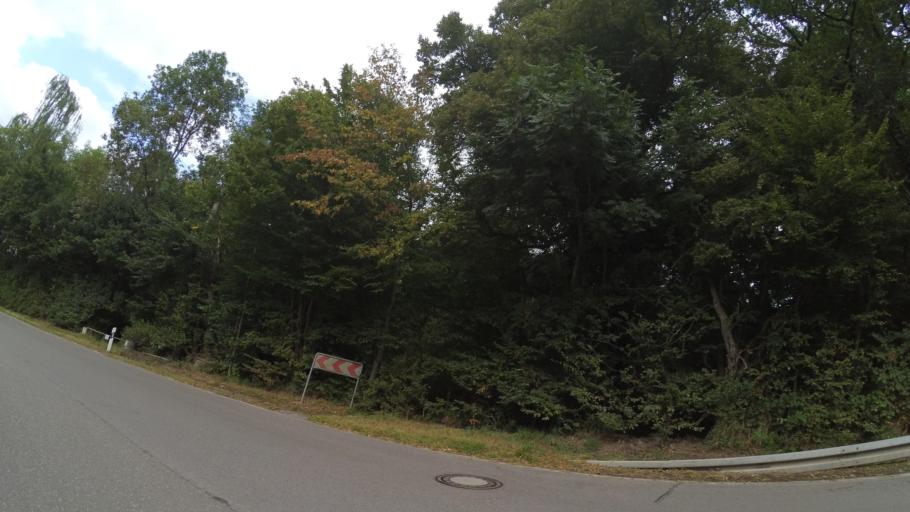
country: DE
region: Saarland
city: Puttlingen
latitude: 49.2601
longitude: 6.8936
